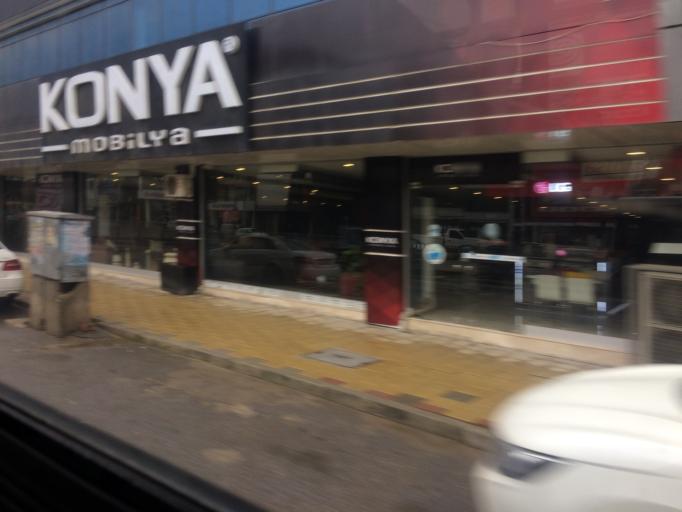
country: TR
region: Izmir
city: Karsiyaka
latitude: 38.4974
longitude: 27.0582
